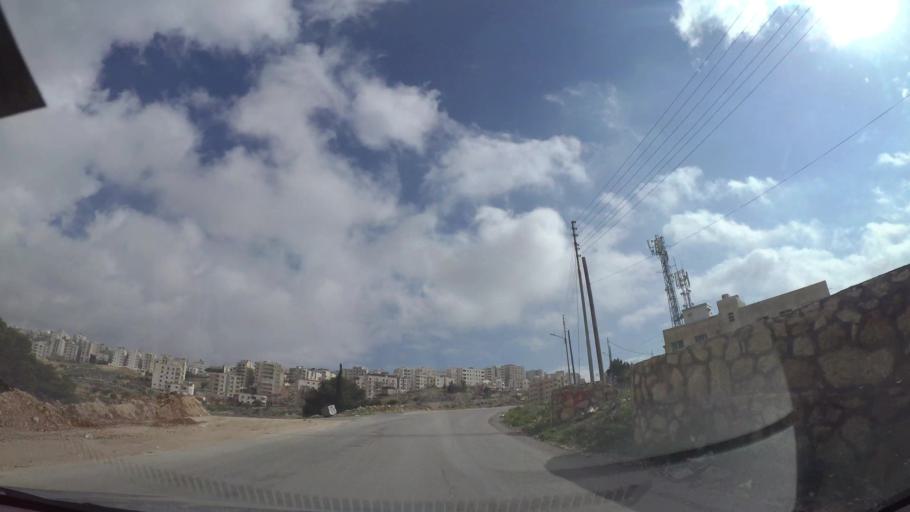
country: JO
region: Amman
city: Al Jubayhah
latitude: 32.0680
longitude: 35.8693
